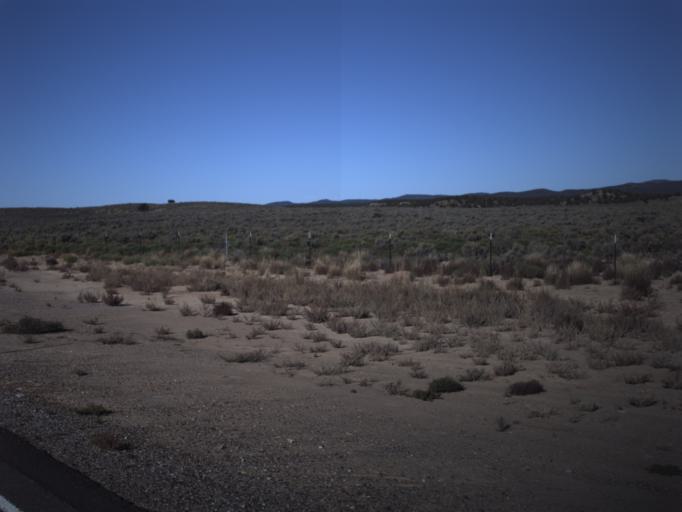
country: US
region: Utah
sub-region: Washington County
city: Enterprise
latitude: 37.7264
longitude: -114.0346
